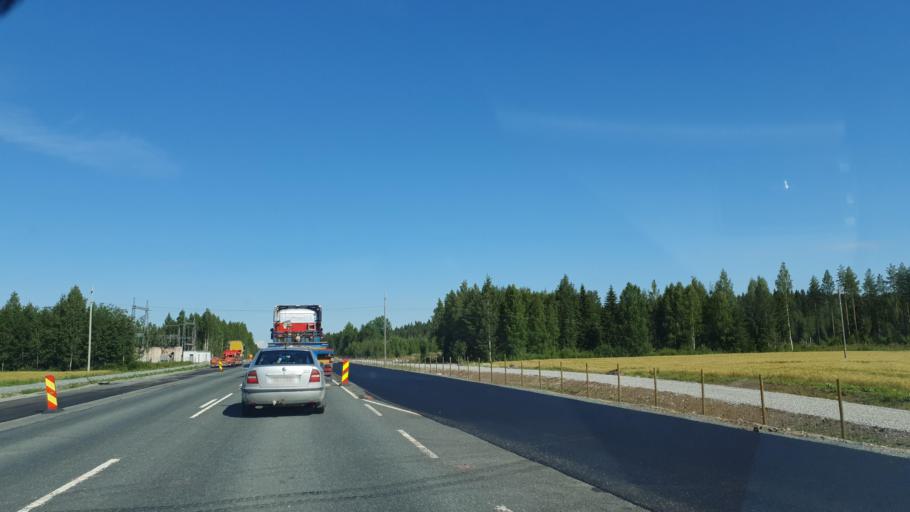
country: FI
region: Northern Savo
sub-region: Ylae-Savo
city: Lapinlahti
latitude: 63.2882
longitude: 27.4547
